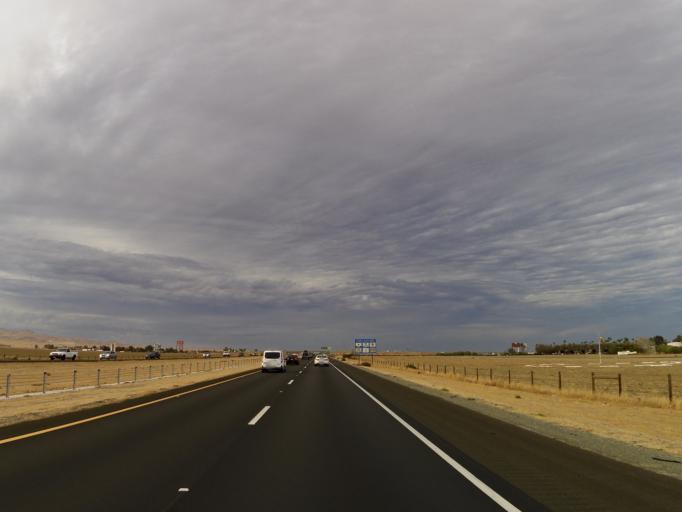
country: US
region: California
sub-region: Fresno County
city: Huron
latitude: 36.2467
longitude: -120.2390
